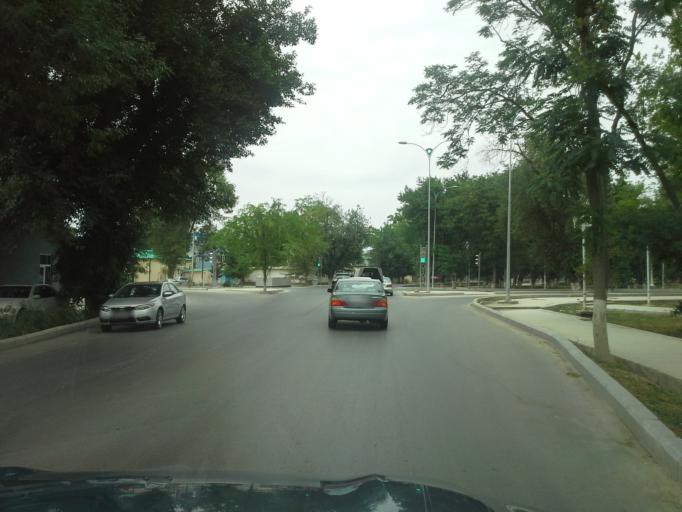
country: TM
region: Ahal
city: Ashgabat
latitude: 37.9488
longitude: 58.3615
